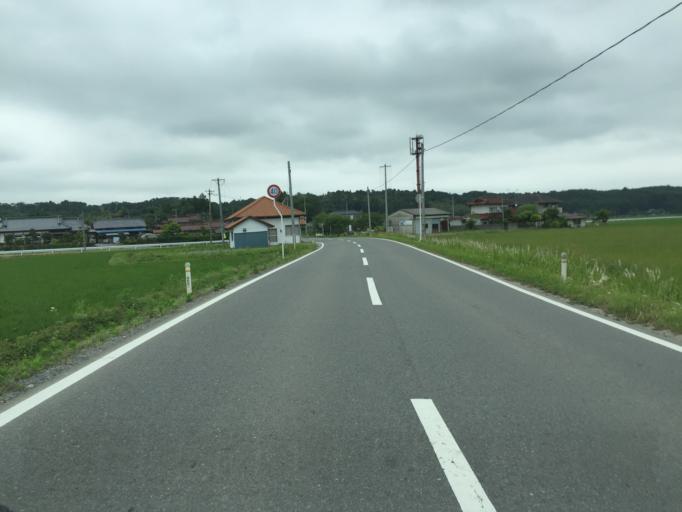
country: JP
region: Miyagi
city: Marumori
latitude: 37.7503
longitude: 140.9153
